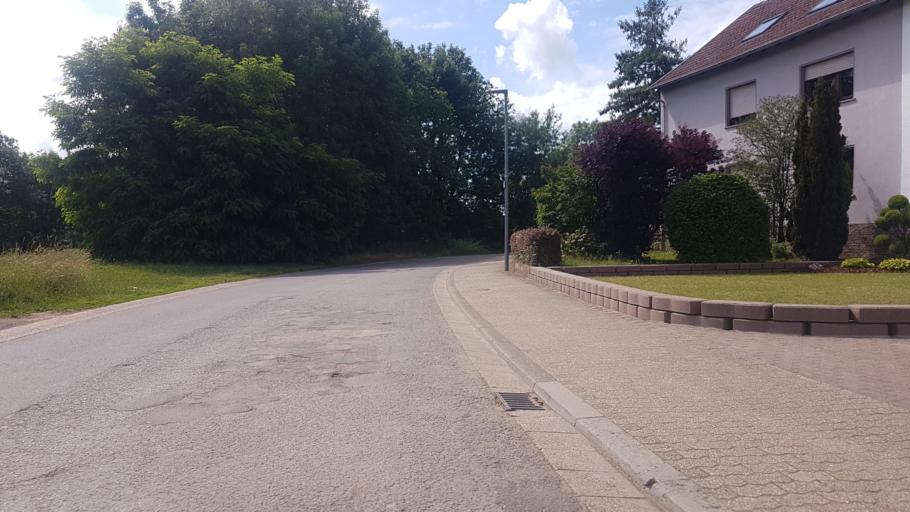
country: DE
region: Saarland
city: Saarlouis
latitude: 49.3077
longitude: 6.7609
